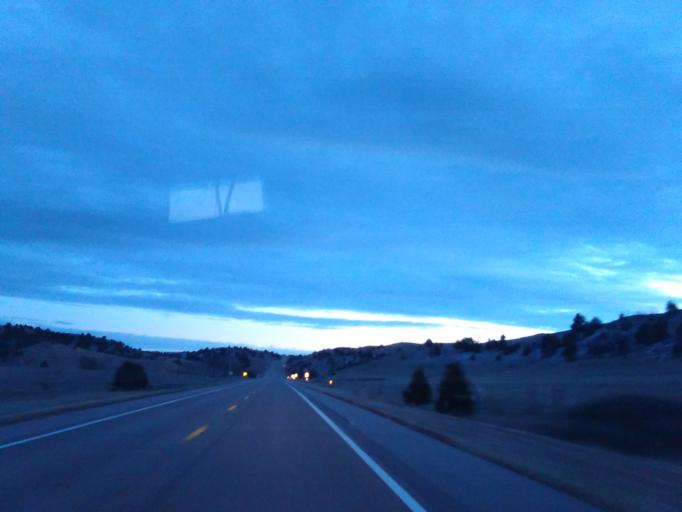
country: US
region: Nebraska
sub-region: Garden County
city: Oshkosh
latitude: 41.2699
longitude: -102.1135
